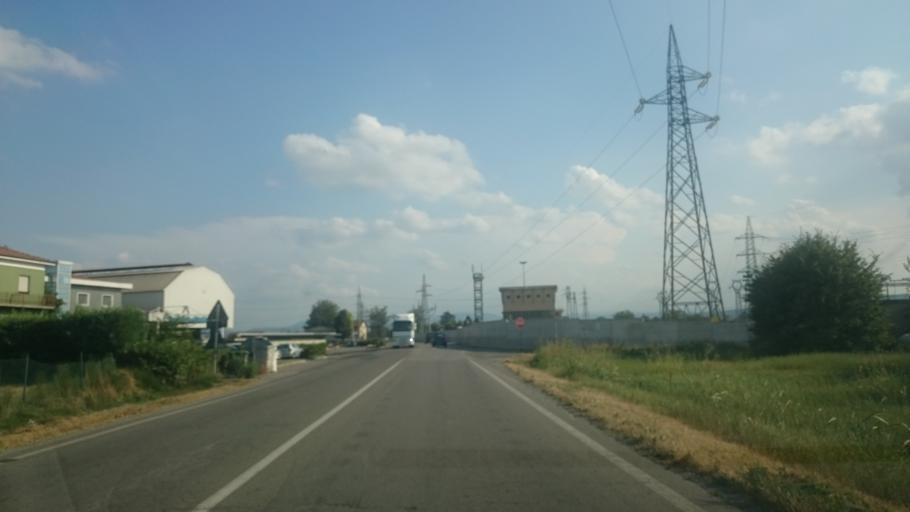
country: IT
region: Emilia-Romagna
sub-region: Provincia di Reggio Emilia
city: Rubiera
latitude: 44.6287
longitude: 10.7774
